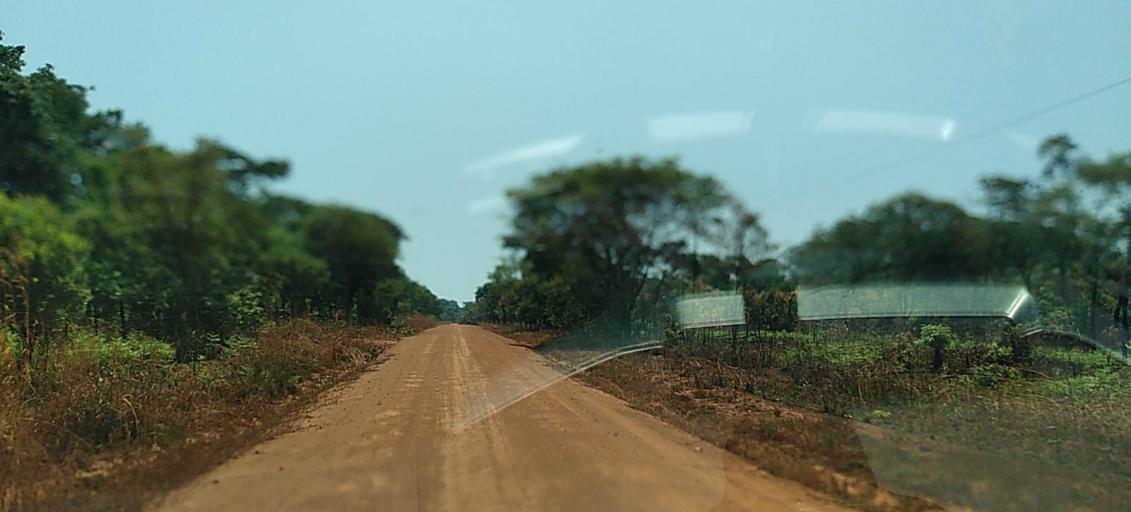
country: ZM
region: North-Western
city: Kansanshi
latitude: -11.9855
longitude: 26.8539
